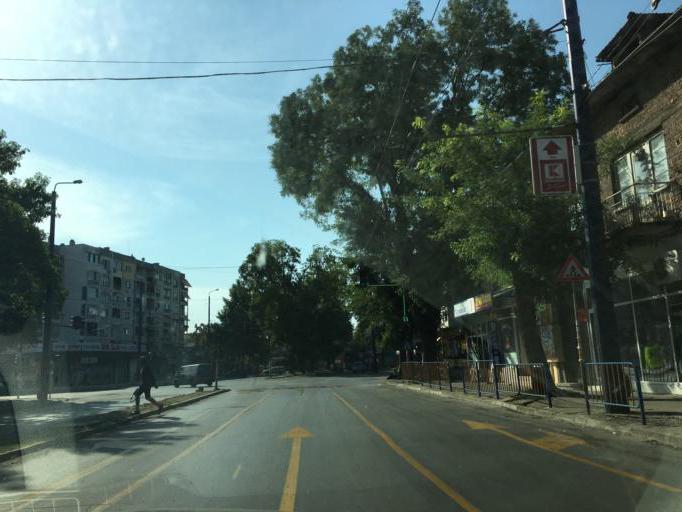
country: BG
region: Pazardzhik
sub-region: Obshtina Pazardzhik
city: Pazardzhik
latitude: 42.1999
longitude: 24.3329
